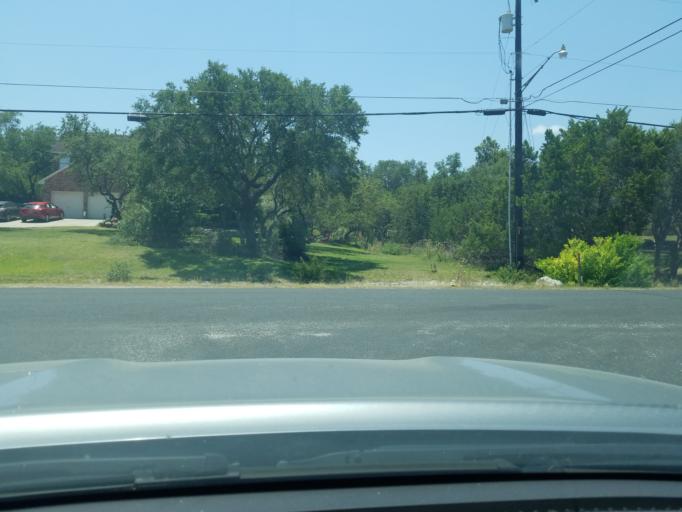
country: US
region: Texas
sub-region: Bexar County
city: Timberwood Park
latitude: 29.6947
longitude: -98.4846
